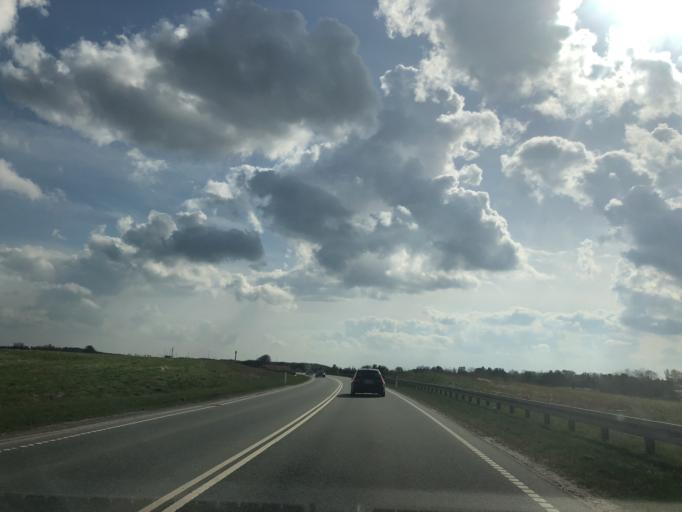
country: DK
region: Capital Region
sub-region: Frederikssund Kommune
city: Slangerup
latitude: 55.8917
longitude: 12.2071
